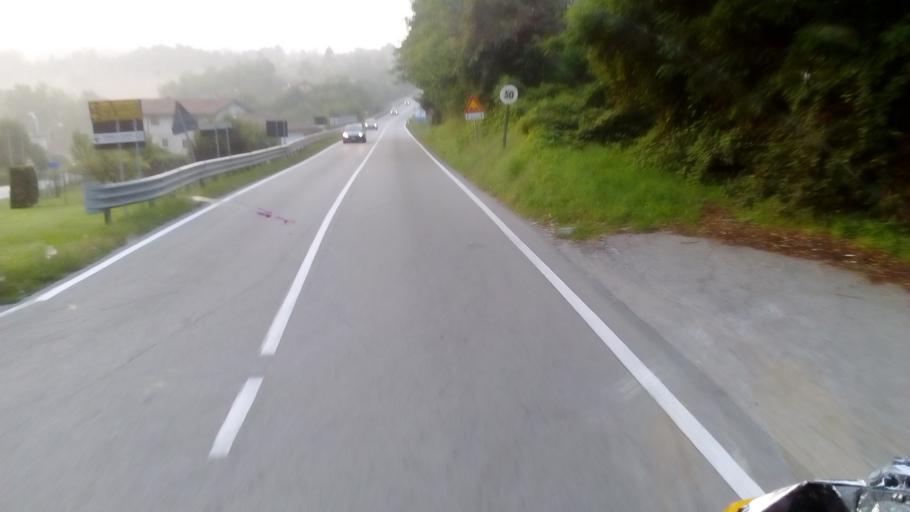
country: IT
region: Piedmont
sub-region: Provincia di Novara
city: Borgo Ticino
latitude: 45.6916
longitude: 8.6036
